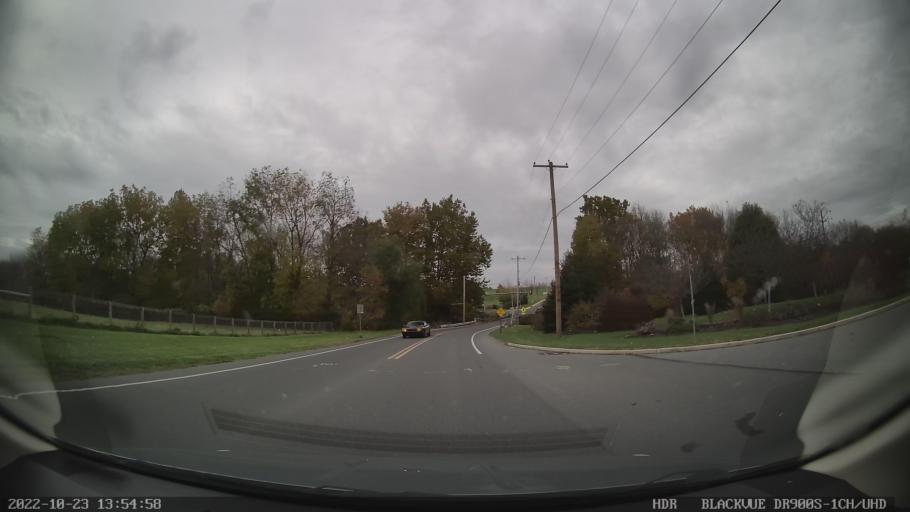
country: US
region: Pennsylvania
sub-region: Northampton County
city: North Catasauqua
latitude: 40.6763
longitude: -75.4617
